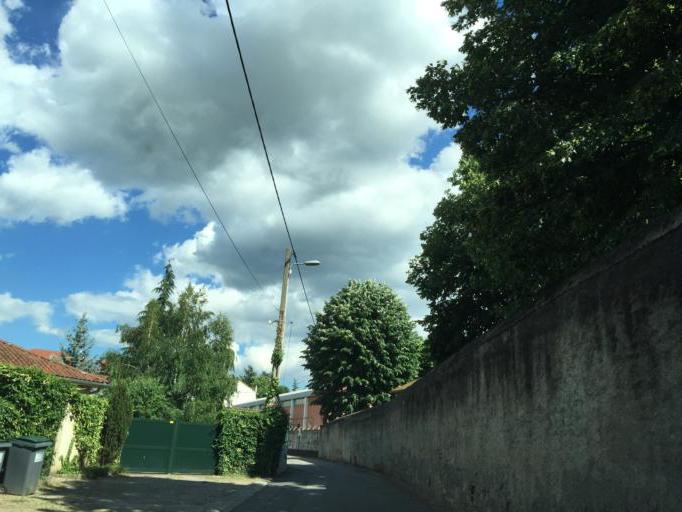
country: FR
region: Rhone-Alpes
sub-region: Departement de la Loire
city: Saint-Chamond
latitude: 45.4727
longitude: 4.5231
